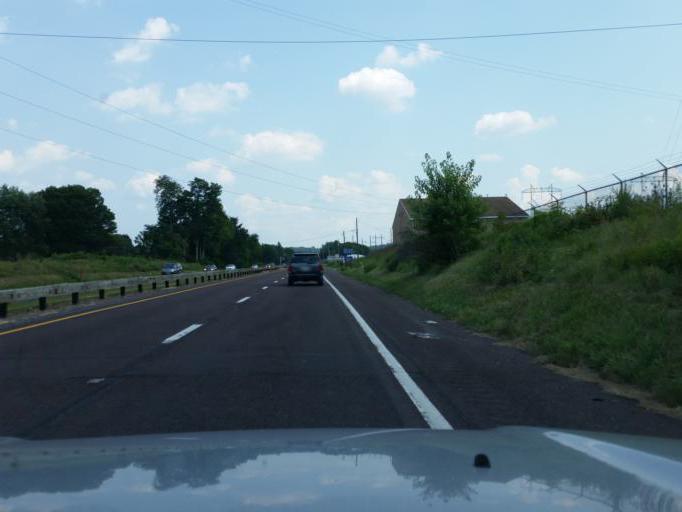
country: US
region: Pennsylvania
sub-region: Dauphin County
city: Hummelstown
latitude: 40.2605
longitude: -76.7221
